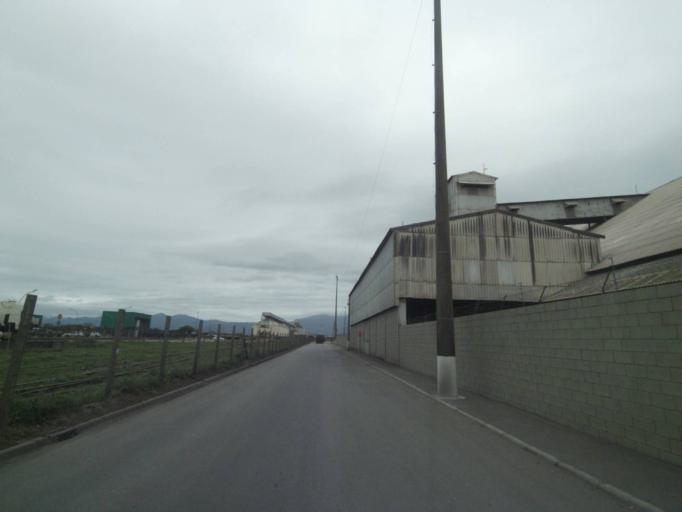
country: BR
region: Parana
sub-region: Paranagua
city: Paranagua
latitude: -25.5375
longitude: -48.5365
